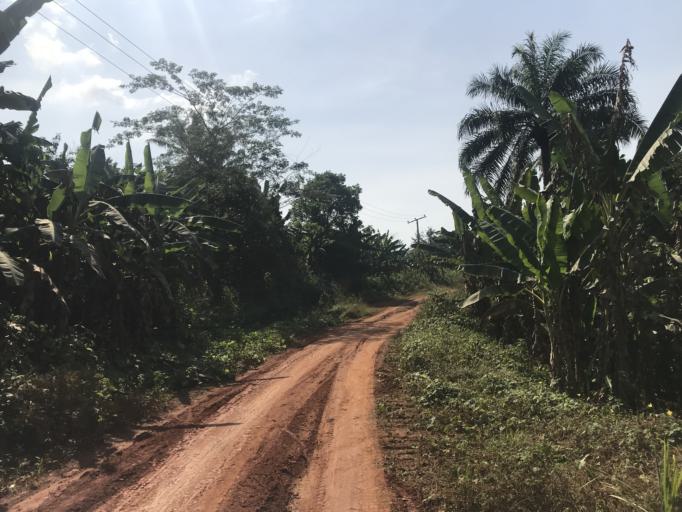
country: NG
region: Osun
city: Osu
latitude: 7.6338
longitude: 4.6681
